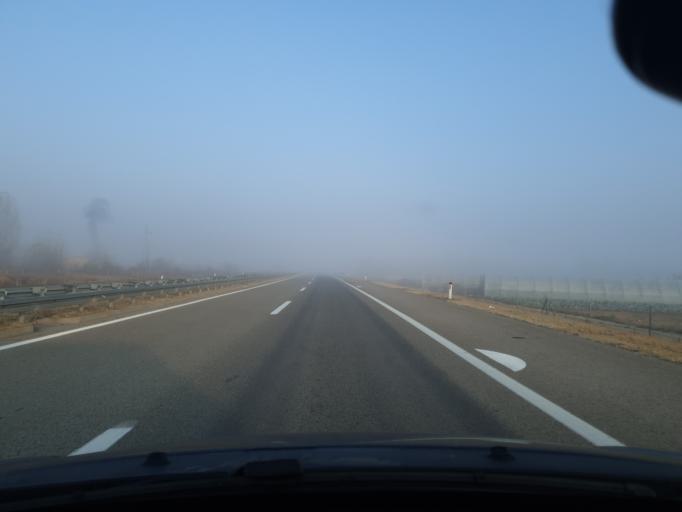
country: RS
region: Central Serbia
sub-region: Jablanicki Okrug
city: Leskovac
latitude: 42.9750
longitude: 22.0354
